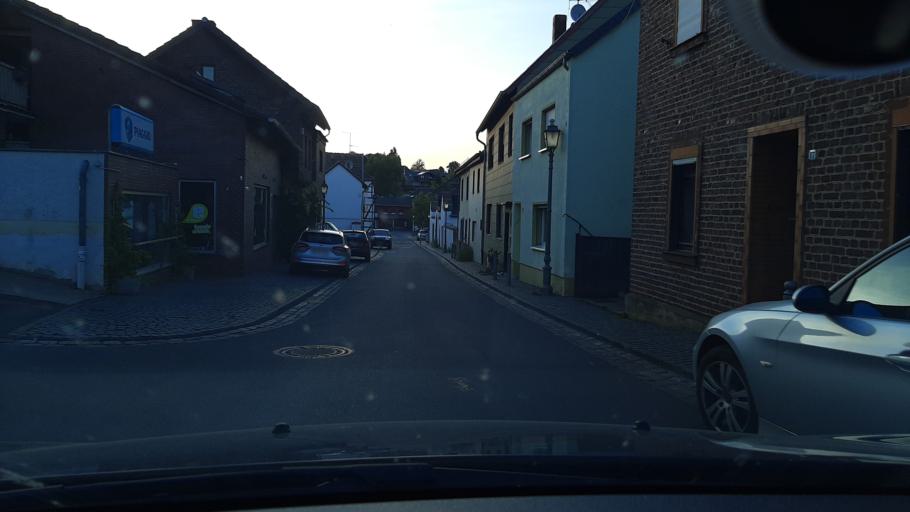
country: DE
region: North Rhine-Westphalia
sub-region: Regierungsbezirk Koln
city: Mechernich
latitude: 50.6096
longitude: 6.6467
